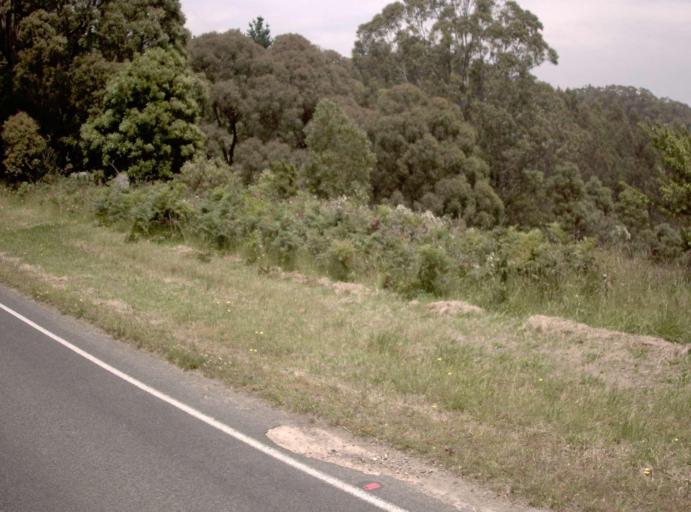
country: AU
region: Victoria
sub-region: Latrobe
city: Traralgon
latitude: -38.3400
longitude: 146.7261
